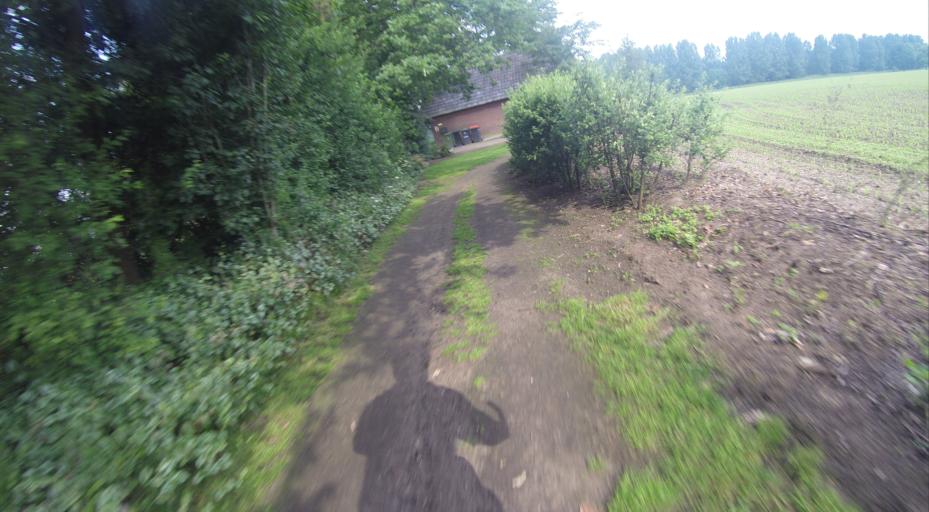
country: NL
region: Gelderland
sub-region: Gemeente Bronckhorst
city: Baak
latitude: 52.0922
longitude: 6.2659
